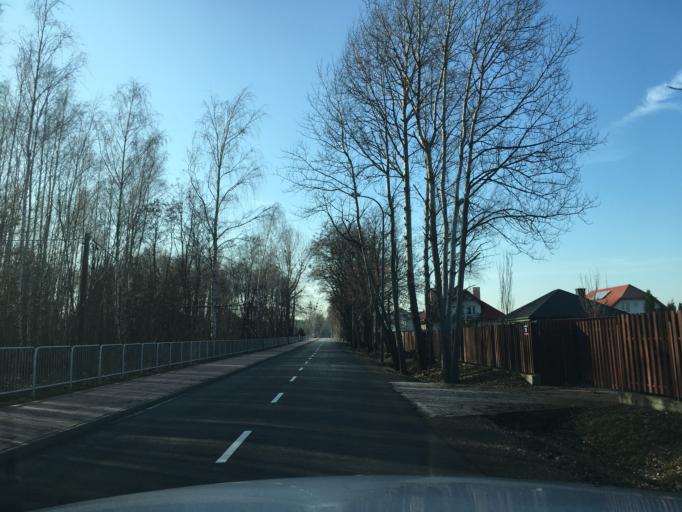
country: PL
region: Lodz Voivodeship
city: Zabia Wola
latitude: 52.0486
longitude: 20.7493
